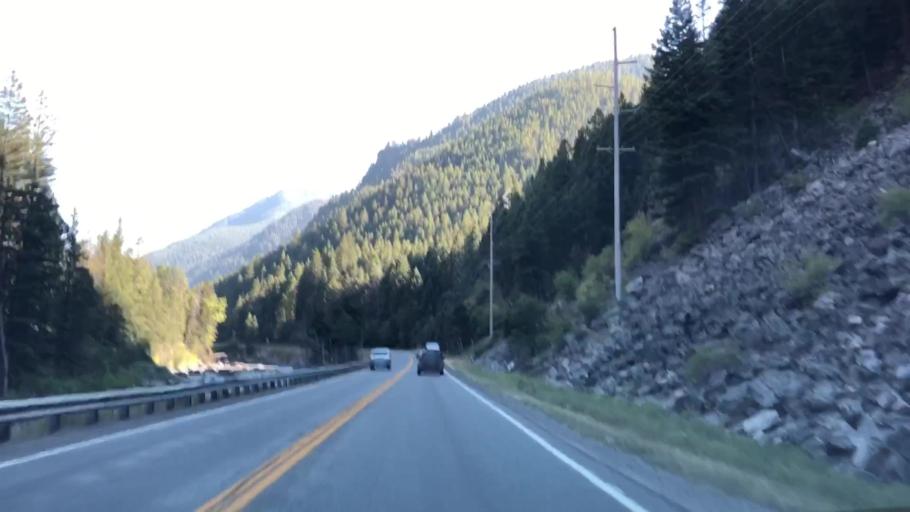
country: US
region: Montana
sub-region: Gallatin County
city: Big Sky
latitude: 45.4176
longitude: -111.2331
